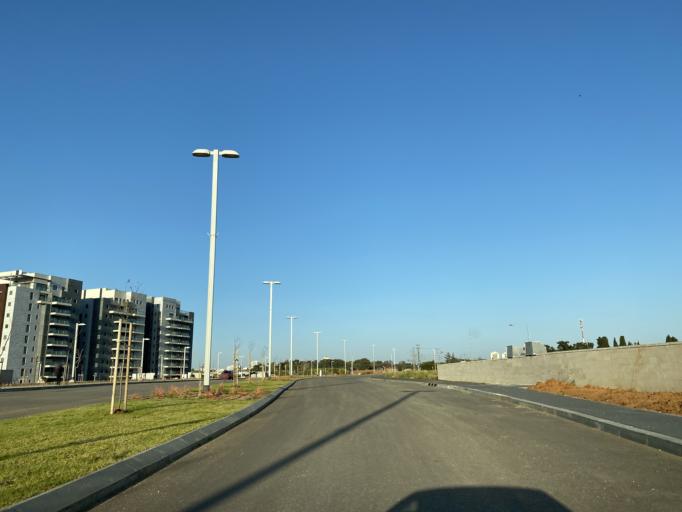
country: IL
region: Tel Aviv
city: Herzliyya
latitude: 32.1557
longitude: 34.8194
